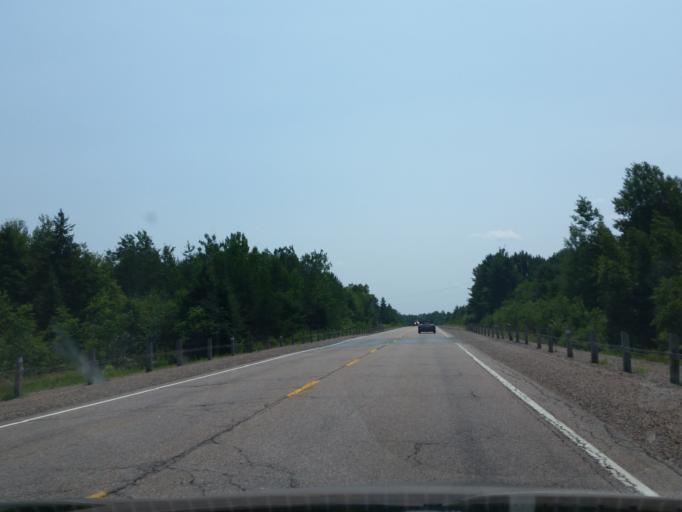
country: CA
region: Ontario
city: Petawawa
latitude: 45.8557
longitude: -77.2841
